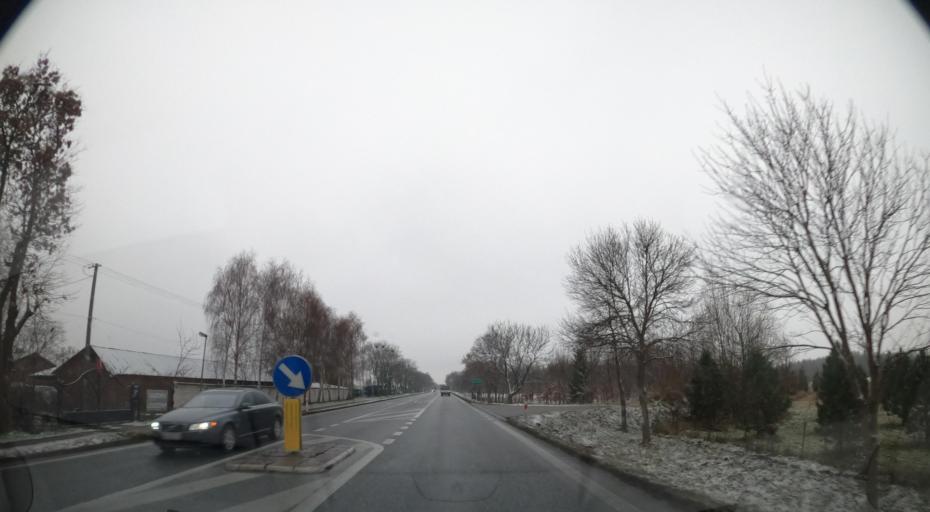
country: PL
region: Masovian Voivodeship
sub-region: Powiat warszawski zachodni
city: Bieniewice
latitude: 52.2013
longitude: 20.5525
